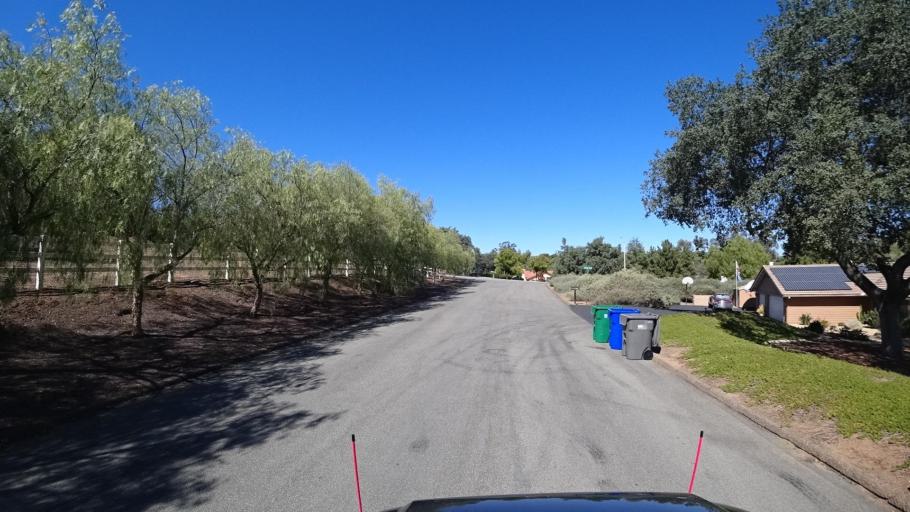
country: US
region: California
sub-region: San Diego County
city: Alpine
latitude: 32.8136
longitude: -116.7807
